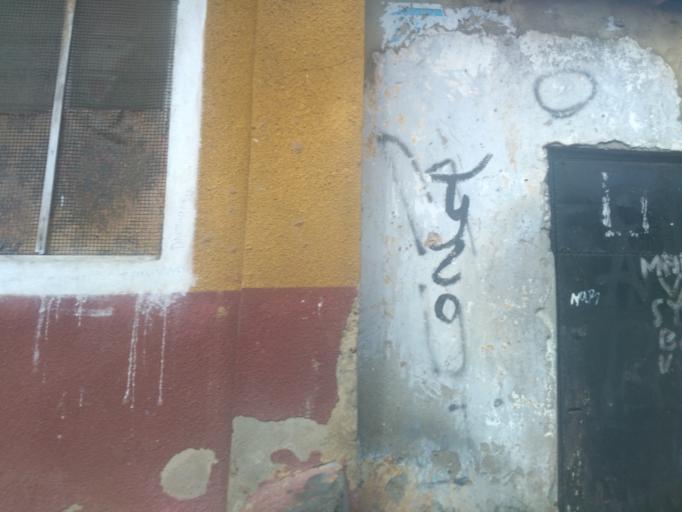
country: TZ
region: Zanzibar Urban/West
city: Zanzibar
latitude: -6.1608
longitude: 39.2056
